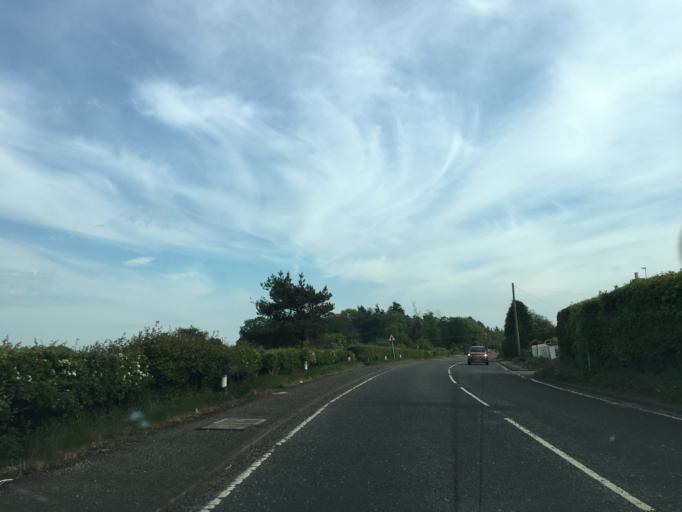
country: GB
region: Scotland
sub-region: Midlothian
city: Loanhead
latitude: 55.8817
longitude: -3.1936
